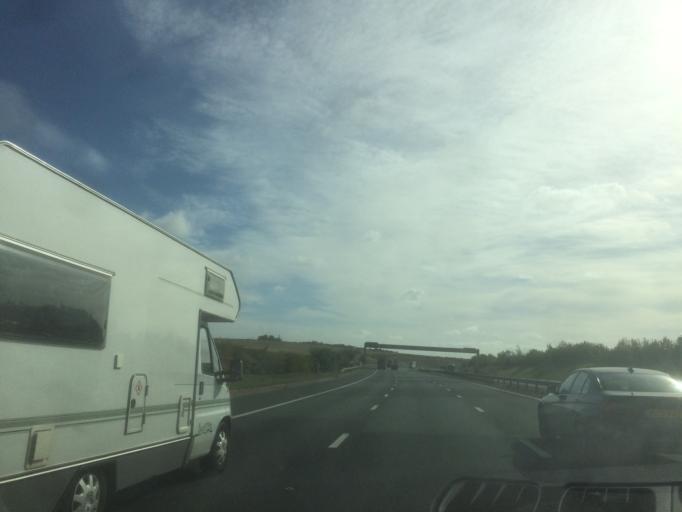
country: GB
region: England
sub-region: City and Borough of Leeds
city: Aberford
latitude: 53.8002
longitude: -1.3323
